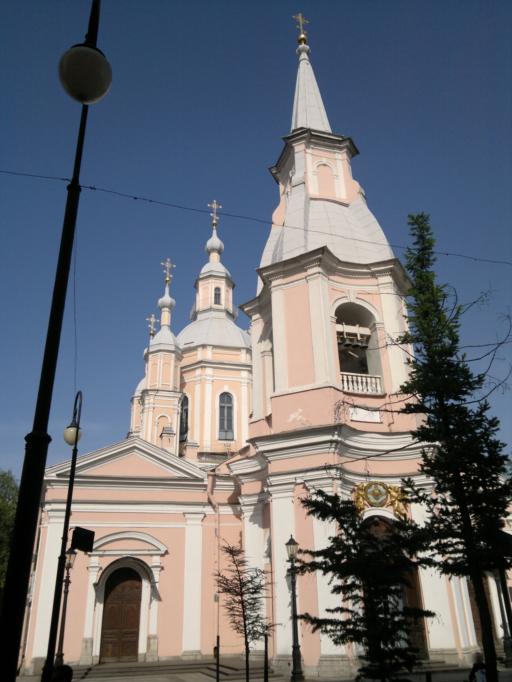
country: RU
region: St.-Petersburg
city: Vasyl'evsky Ostrov
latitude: 59.9396
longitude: 30.2826
